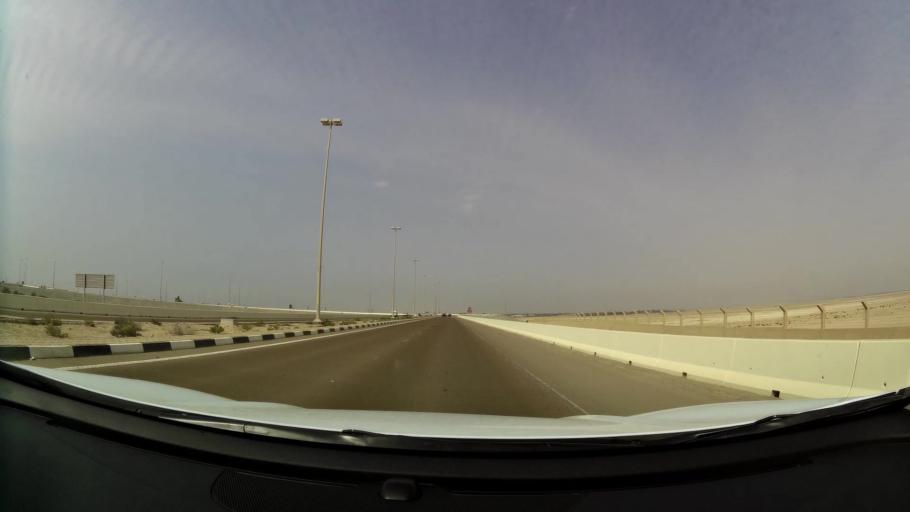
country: AE
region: Abu Dhabi
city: Abu Dhabi
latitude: 24.5609
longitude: 54.6990
